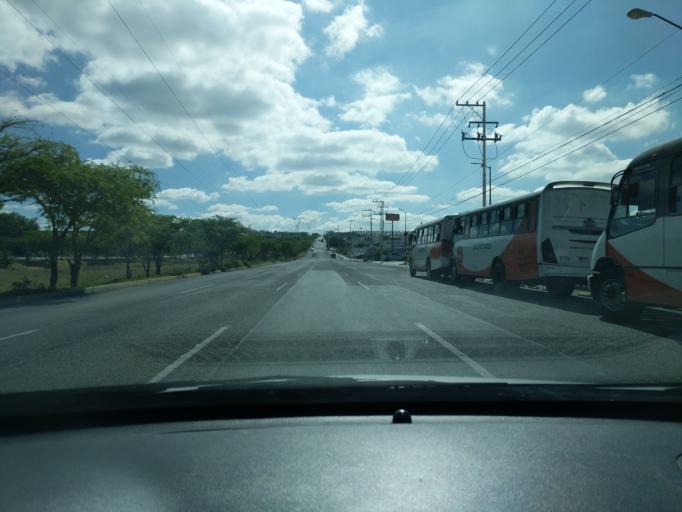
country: MX
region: Queretaro
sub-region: Queretaro
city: Patria Nueva
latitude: 20.6400
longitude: -100.4970
